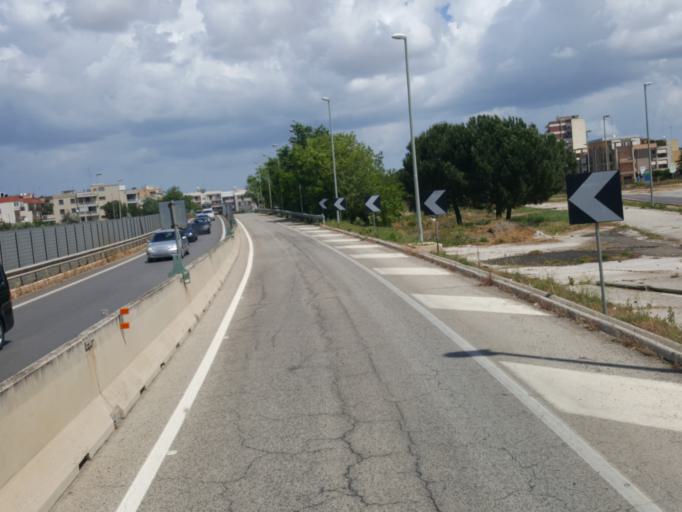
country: IT
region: Apulia
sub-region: Provincia di Bari
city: Modugno
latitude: 41.0850
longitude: 16.7726
